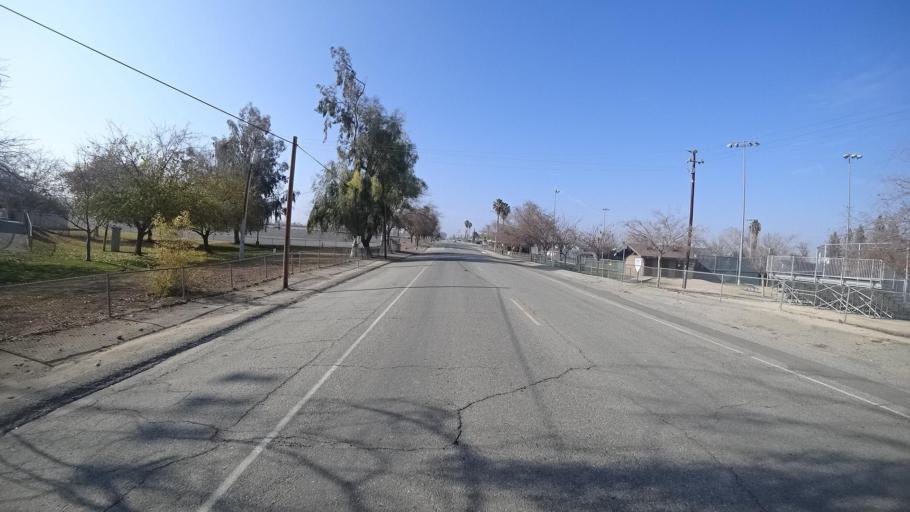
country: US
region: California
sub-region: Kern County
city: Ford City
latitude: 35.1545
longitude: -119.4411
